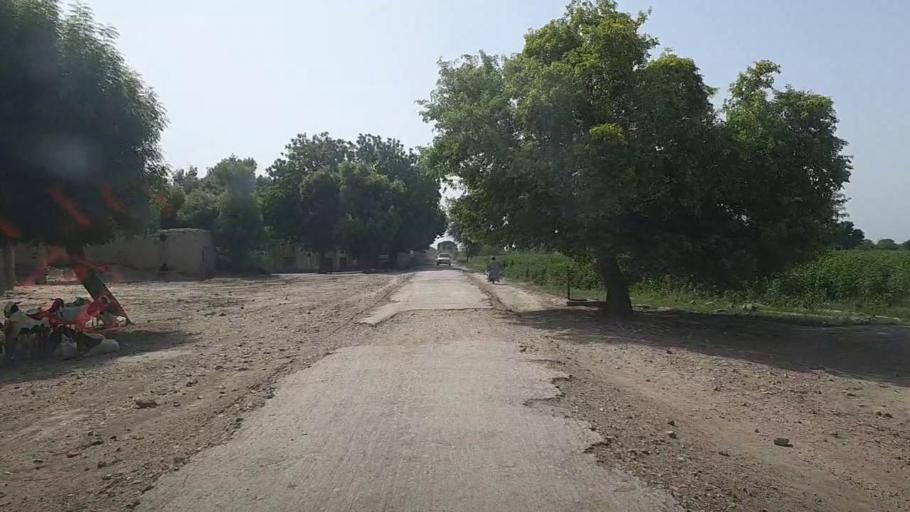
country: PK
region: Sindh
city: Pad Idan
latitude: 26.7636
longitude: 68.3310
